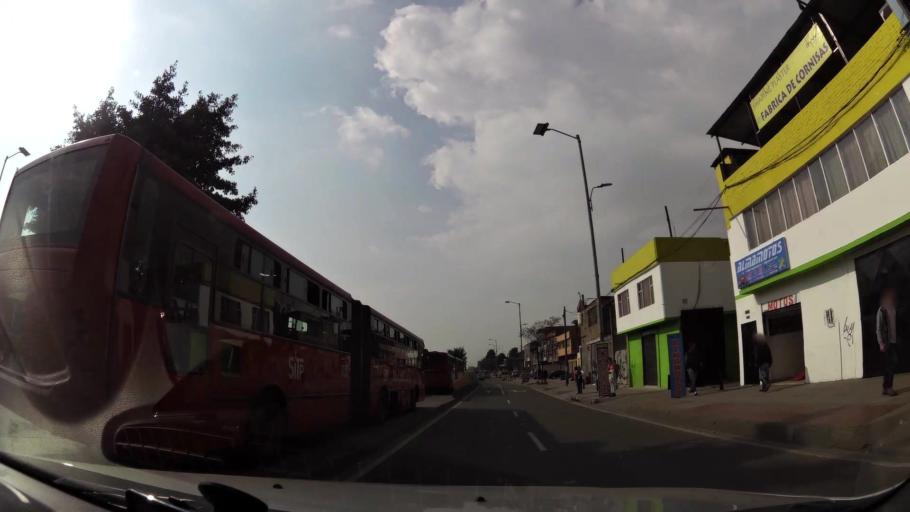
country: CO
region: Bogota D.C.
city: Bogota
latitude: 4.5599
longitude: -74.1236
